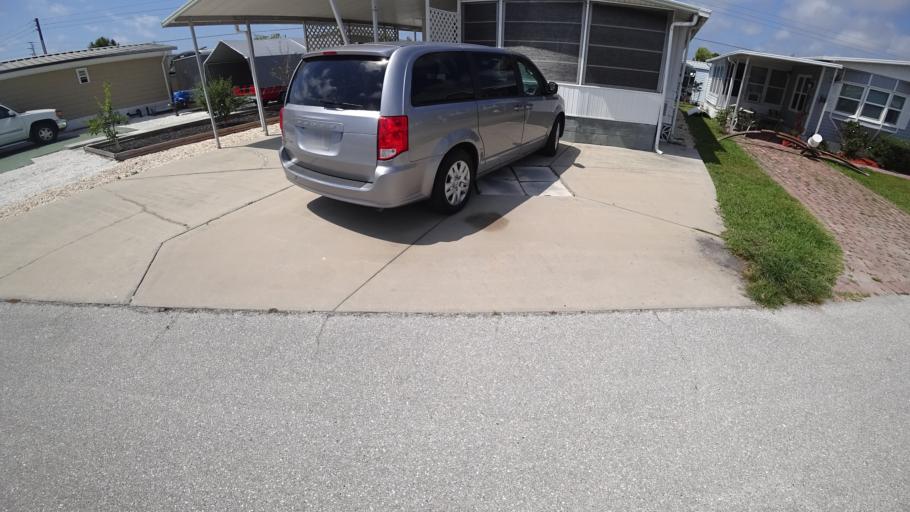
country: US
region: Florida
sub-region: Manatee County
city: Bayshore Gardens
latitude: 27.4236
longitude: -82.5794
